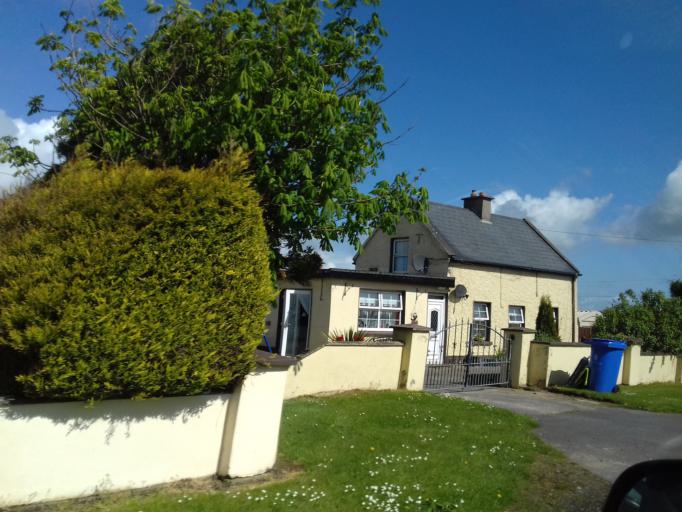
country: IE
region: Leinster
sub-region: Loch Garman
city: Castlebridge
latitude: 52.3791
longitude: -6.4259
